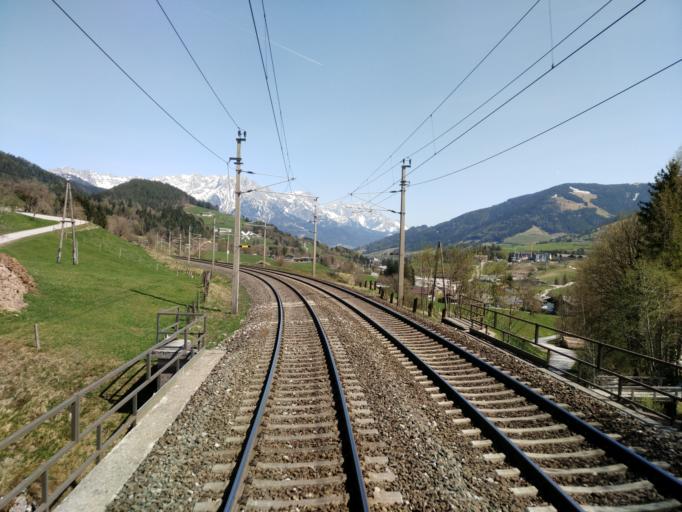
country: AT
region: Salzburg
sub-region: Politischer Bezirk Zell am See
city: Leogang
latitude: 47.4418
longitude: 12.7229
